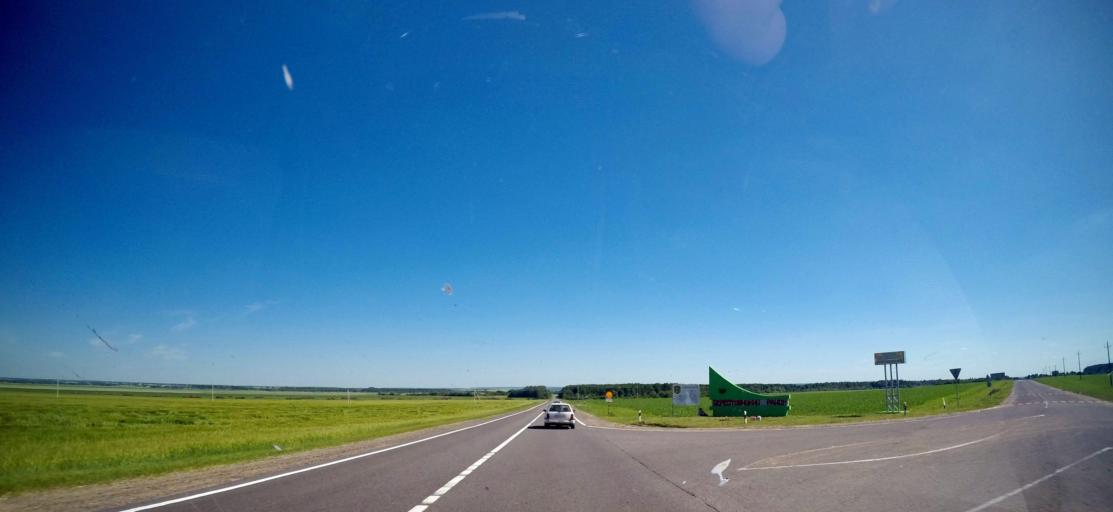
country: BY
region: Grodnenskaya
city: Indura
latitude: 53.4316
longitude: 23.9364
